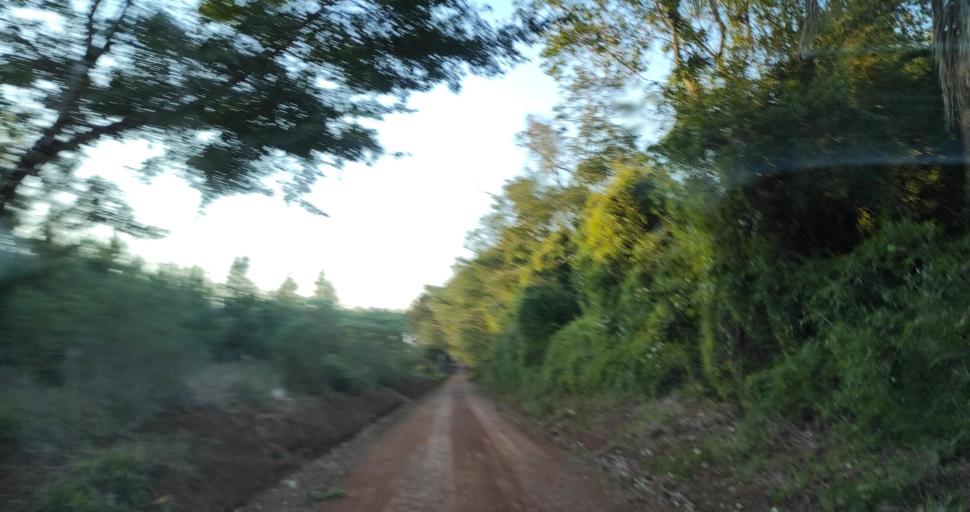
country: AR
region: Misiones
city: Capiovi
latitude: -26.8800
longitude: -55.1077
